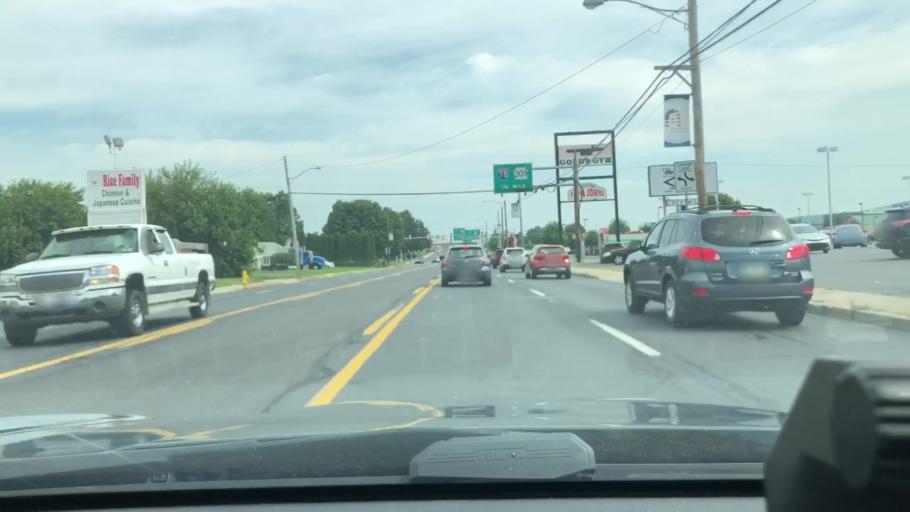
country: US
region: Pennsylvania
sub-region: Lehigh County
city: Emmaus
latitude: 40.5597
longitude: -75.4873
